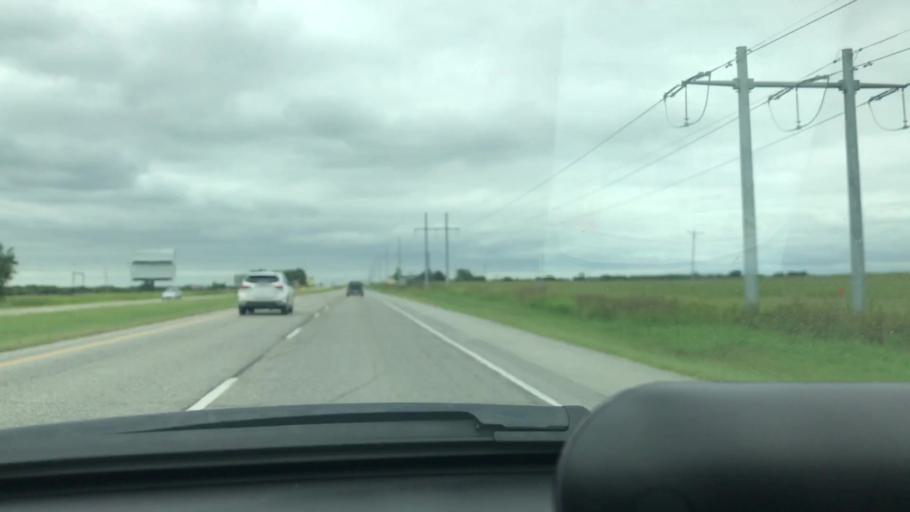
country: US
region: Oklahoma
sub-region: Wagoner County
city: Wagoner
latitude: 36.0085
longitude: -95.3687
